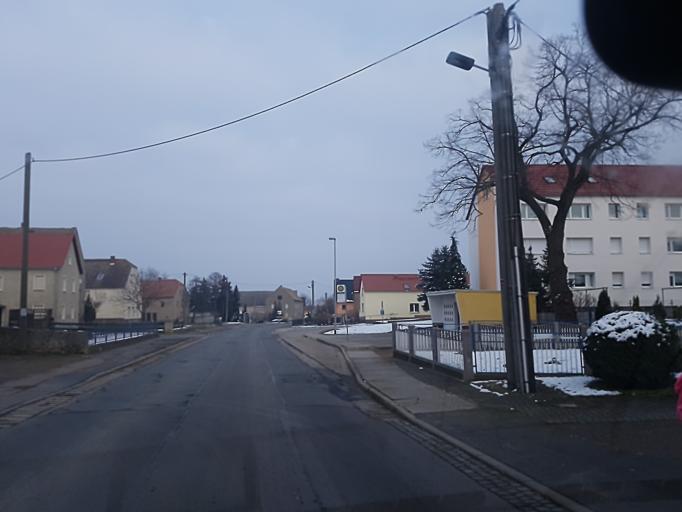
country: DE
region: Saxony
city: Cavertitz
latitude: 51.3655
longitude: 13.1444
